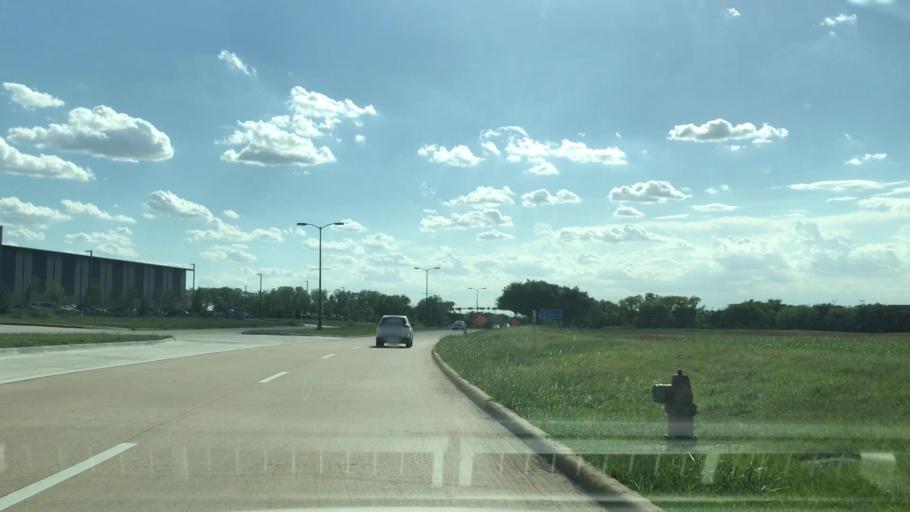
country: US
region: Texas
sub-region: Tarrant County
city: Euless
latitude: 32.8531
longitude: -97.0298
